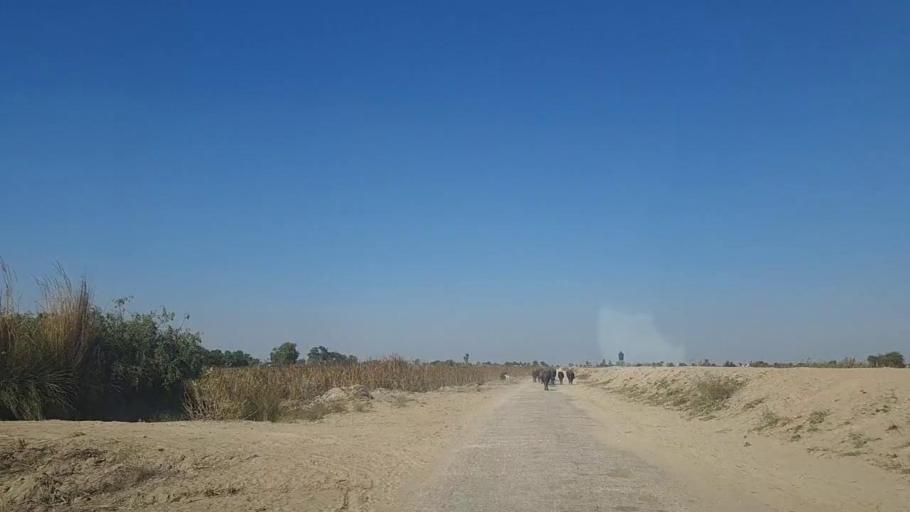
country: PK
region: Sindh
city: Sanghar
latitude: 26.2114
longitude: 68.9293
